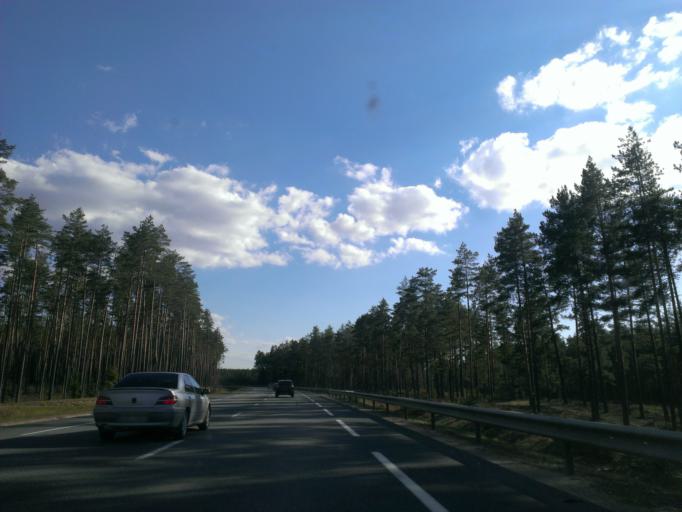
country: LV
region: Saulkrastu
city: Saulkrasti
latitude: 57.2858
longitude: 24.4335
